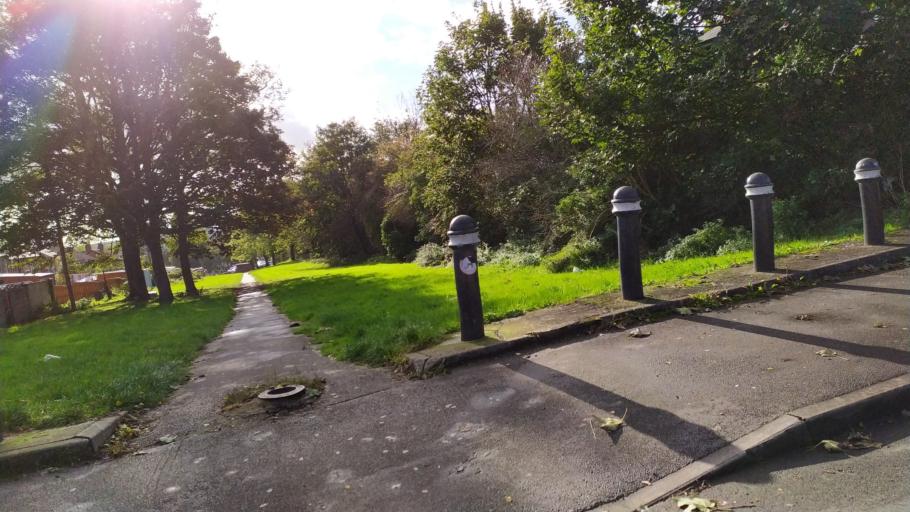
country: GB
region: England
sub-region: City and Borough of Leeds
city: Chapel Allerton
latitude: 53.8160
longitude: -1.5367
